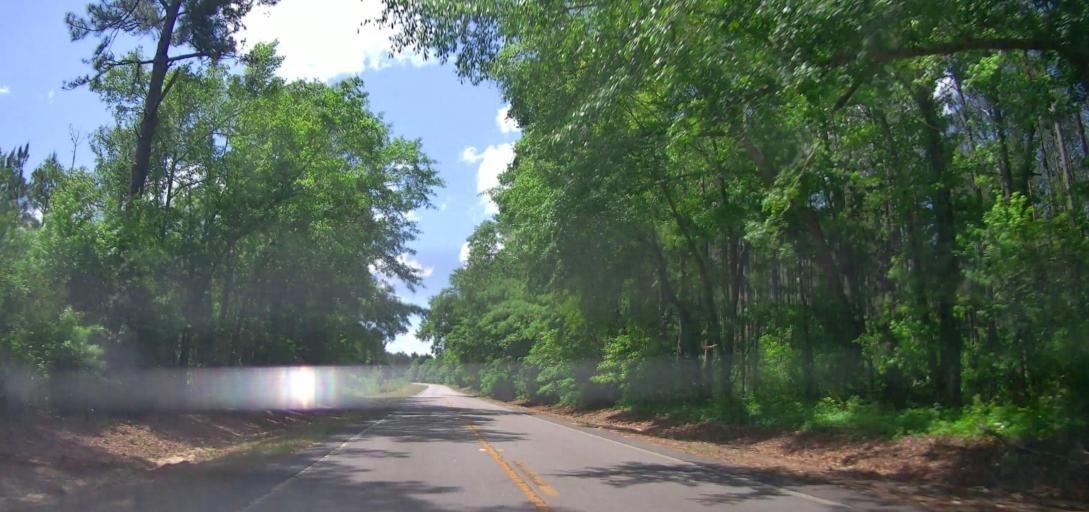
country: US
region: Georgia
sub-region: Bleckley County
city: Cochran
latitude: 32.4610
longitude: -83.2843
